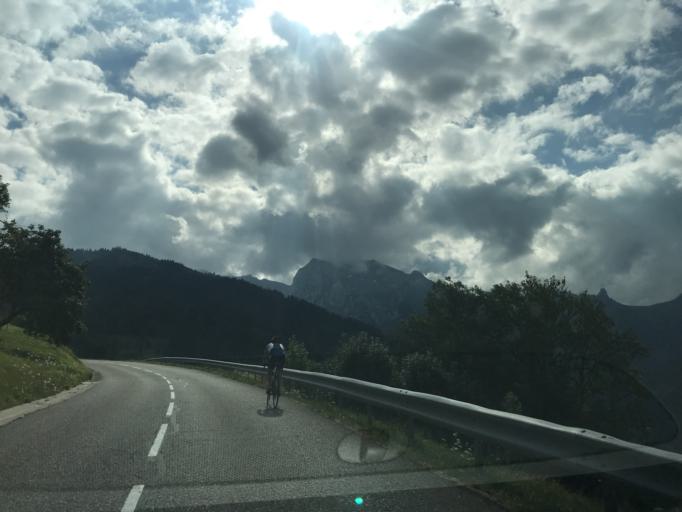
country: FR
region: Rhone-Alpes
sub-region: Departement de la Haute-Savoie
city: Thones
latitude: 45.8622
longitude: 6.3762
